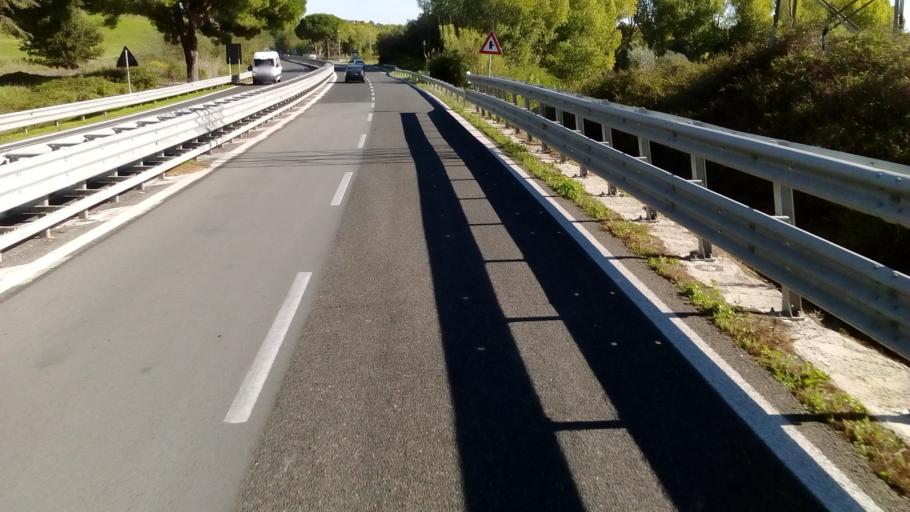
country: IT
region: Latium
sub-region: Provincia di Viterbo
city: Montalto di Castro
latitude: 42.3579
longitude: 11.5878
